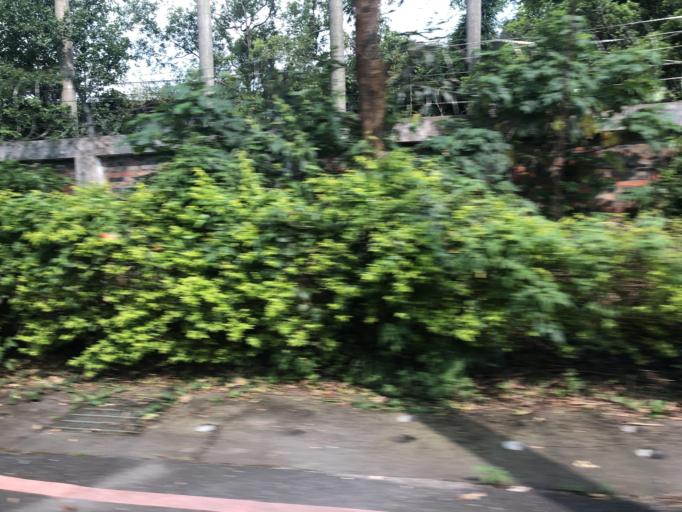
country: TW
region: Taiwan
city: Daxi
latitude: 24.9040
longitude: 121.3566
